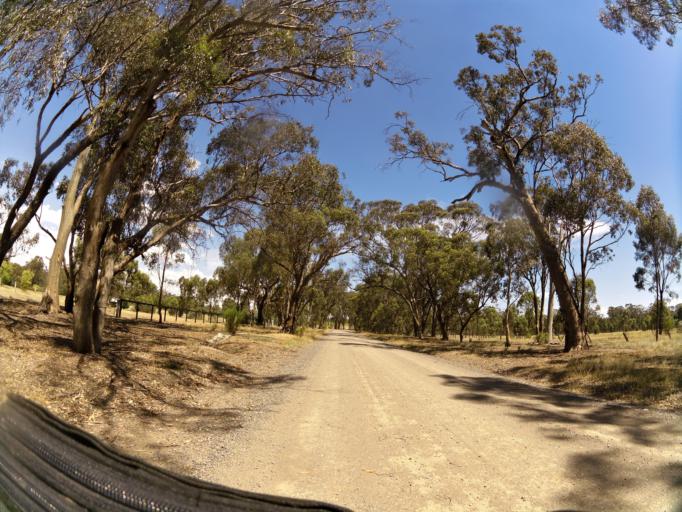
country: AU
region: Victoria
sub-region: Campaspe
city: Kyabram
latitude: -36.8155
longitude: 145.0796
